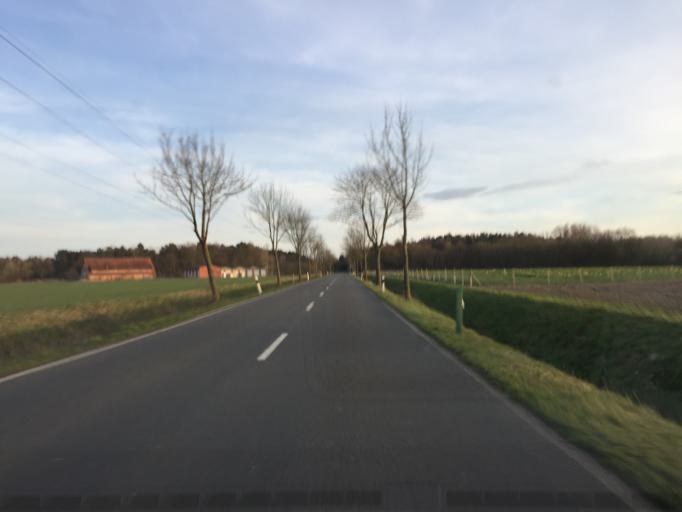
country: DE
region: Lower Saxony
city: Neustadt am Rubenberge
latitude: 52.4974
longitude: 9.4859
